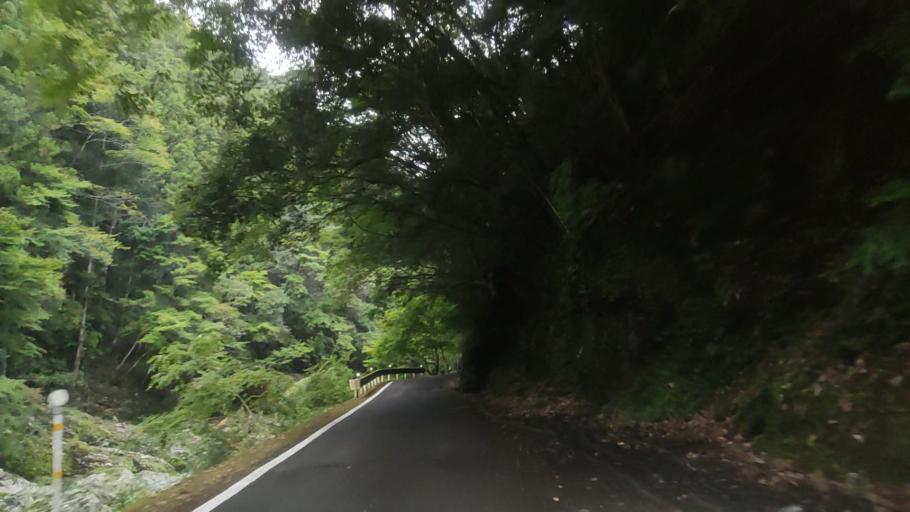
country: JP
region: Wakayama
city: Koya
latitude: 34.2529
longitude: 135.6518
